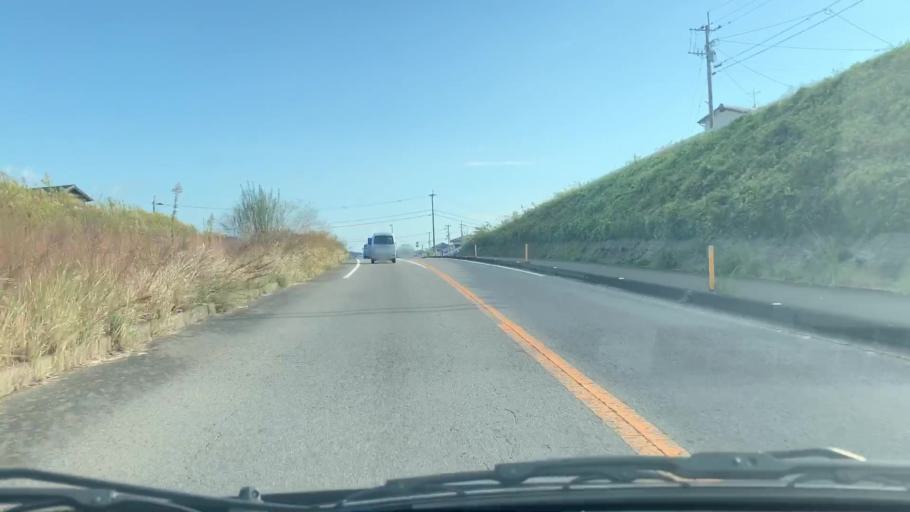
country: JP
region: Saga Prefecture
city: Kashima
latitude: 33.1006
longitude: 130.0877
